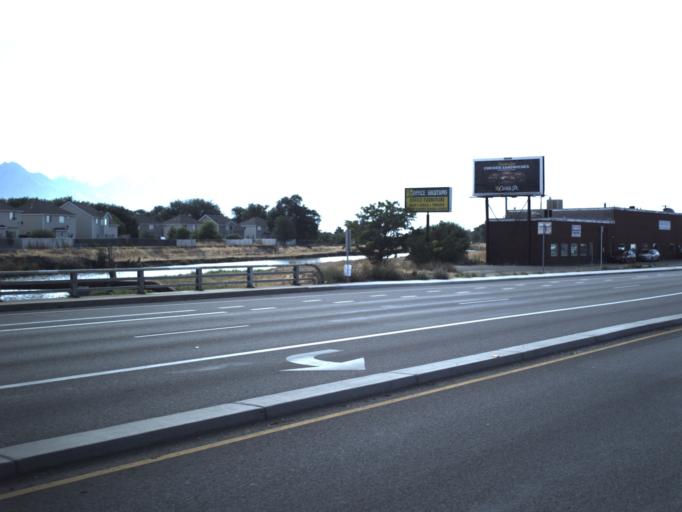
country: US
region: Utah
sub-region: Salt Lake County
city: Salt Lake City
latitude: 40.7403
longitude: -111.9391
